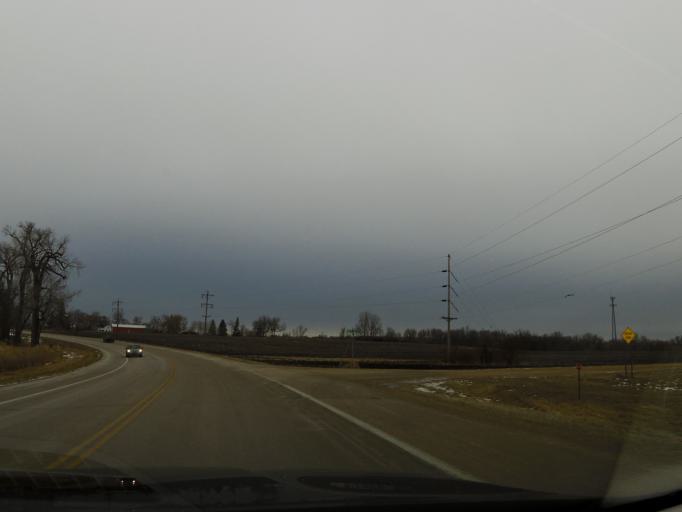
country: US
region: Minnesota
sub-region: Carver County
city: Watertown
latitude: 44.9303
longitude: -93.8324
